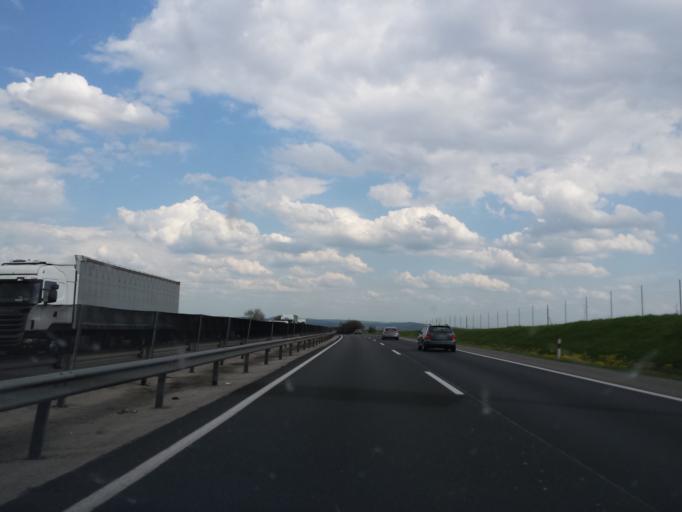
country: HU
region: Fejer
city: Many
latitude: 47.5076
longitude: 18.6833
